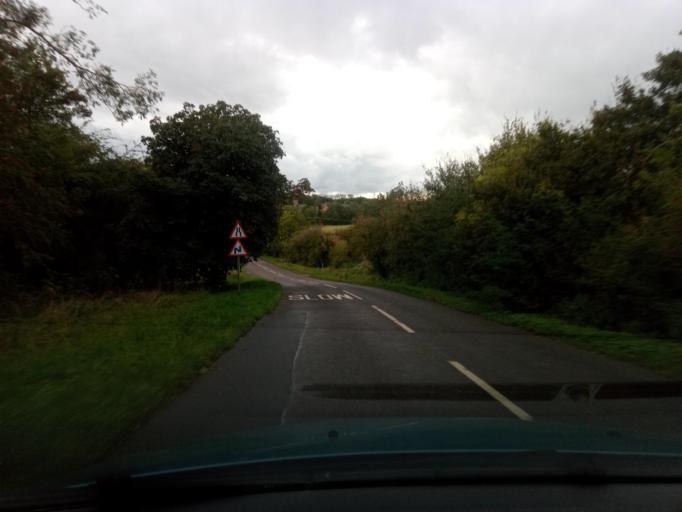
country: GB
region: England
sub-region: Leicestershire
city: Sileby
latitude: 52.7494
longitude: -1.0777
